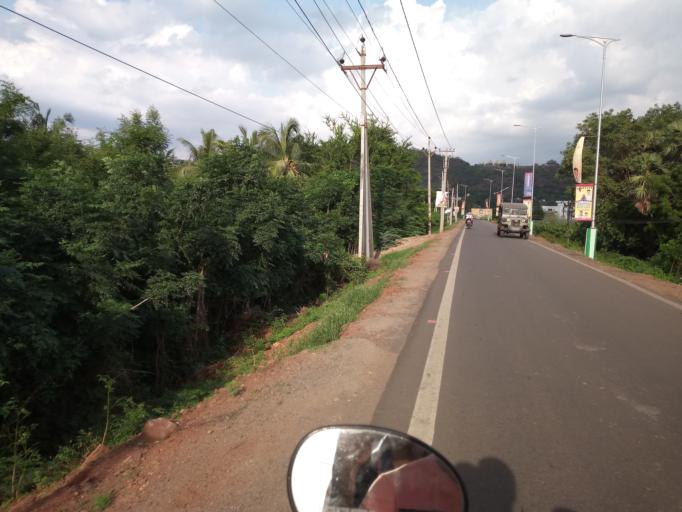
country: IN
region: Andhra Pradesh
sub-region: Guntur
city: Tadepalle
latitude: 16.5002
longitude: 80.5944
